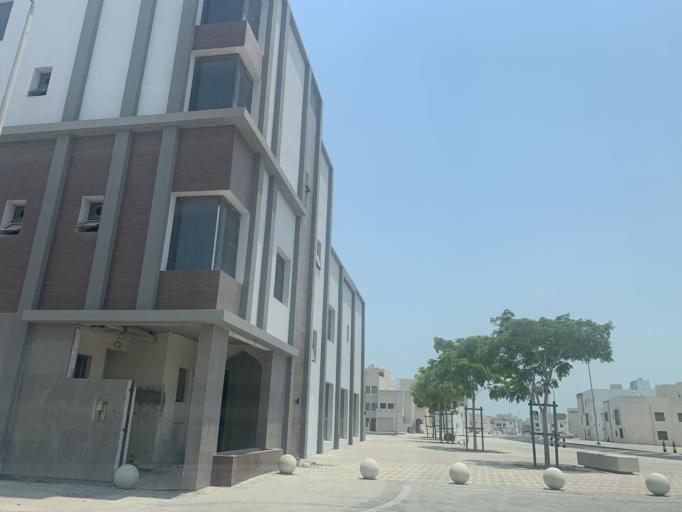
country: BH
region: Muharraq
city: Al Hadd
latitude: 26.2362
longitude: 50.6731
